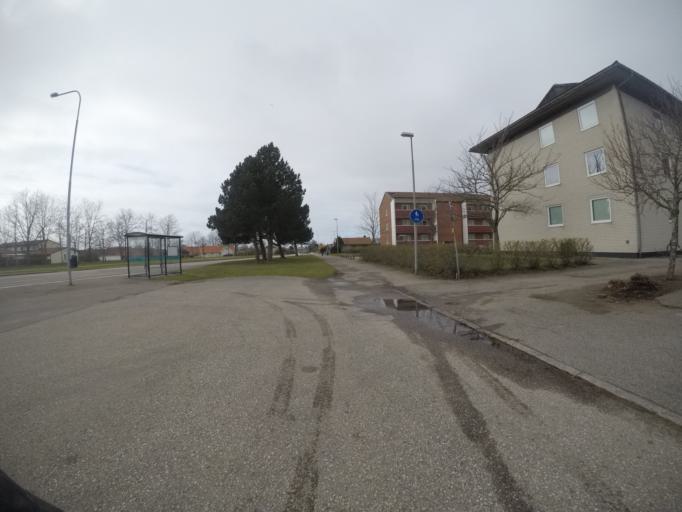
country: SE
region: Halland
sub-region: Laholms Kommun
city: Laholm
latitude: 56.5036
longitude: 13.0466
